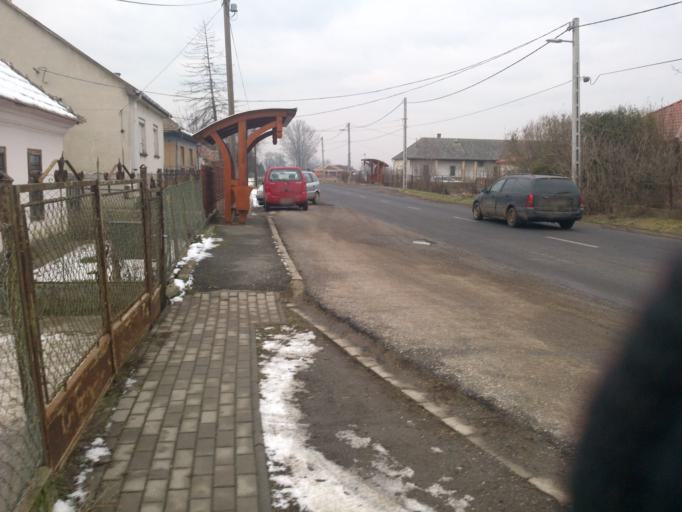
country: HU
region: Borsod-Abauj-Zemplen
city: Encs
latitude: 48.3181
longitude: 21.1560
